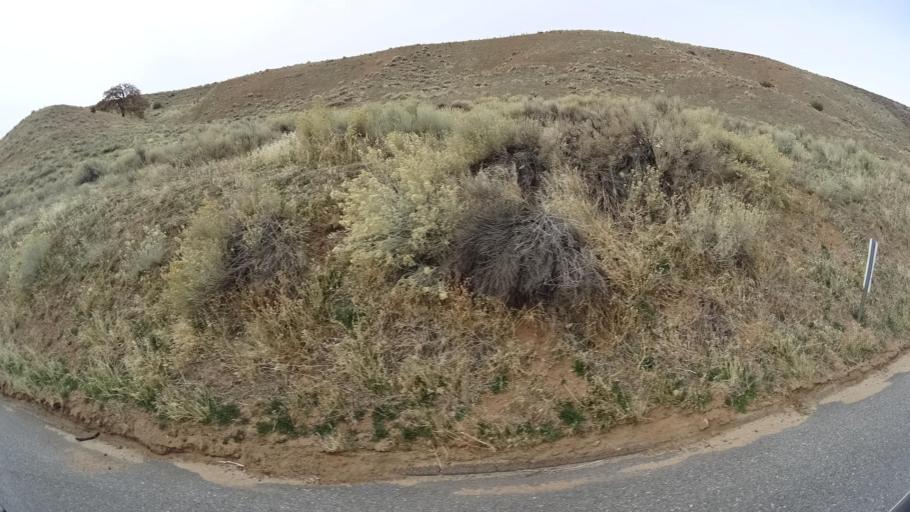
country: US
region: California
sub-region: Kern County
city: Tehachapi
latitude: 35.0751
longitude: -118.3973
